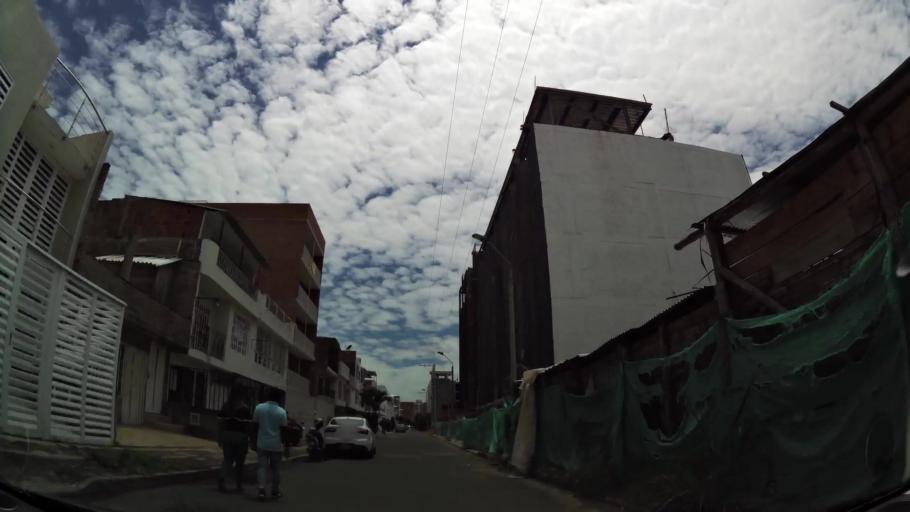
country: CO
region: Valle del Cauca
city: Cali
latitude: 3.3785
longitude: -76.5159
